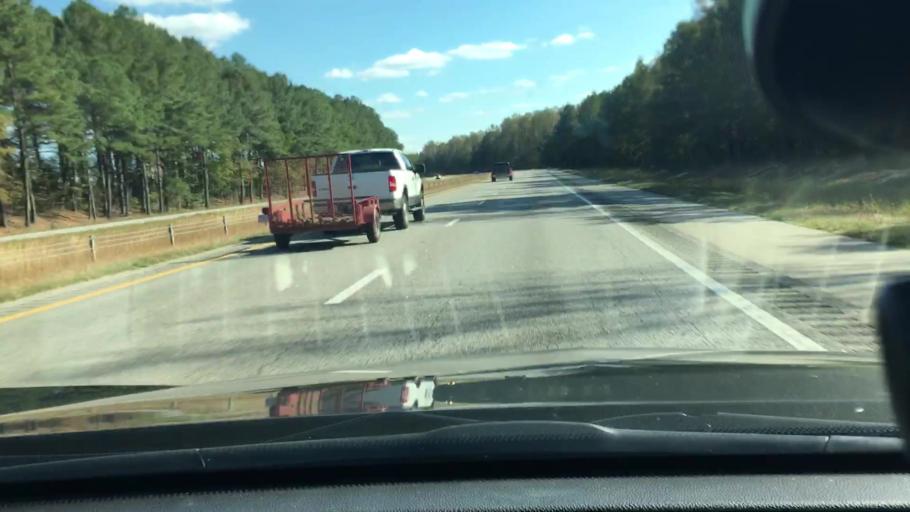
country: US
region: North Carolina
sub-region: Wilson County
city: Wilson
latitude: 35.6749
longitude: -77.8340
